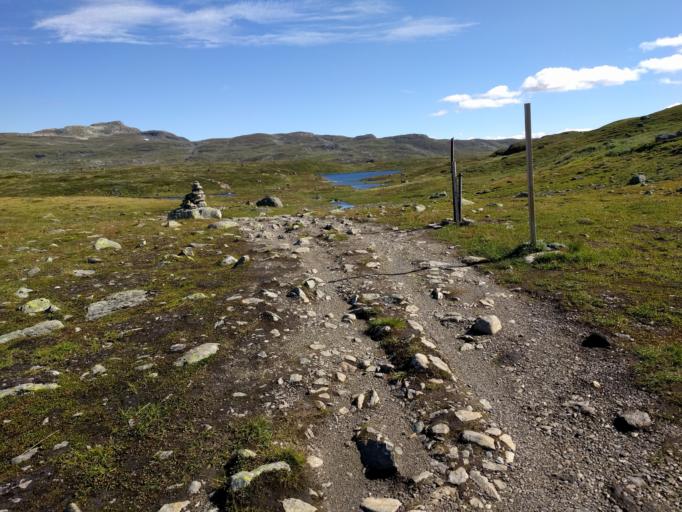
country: NO
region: Aust-Agder
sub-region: Bykle
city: Hovden
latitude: 59.8270
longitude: 7.2059
